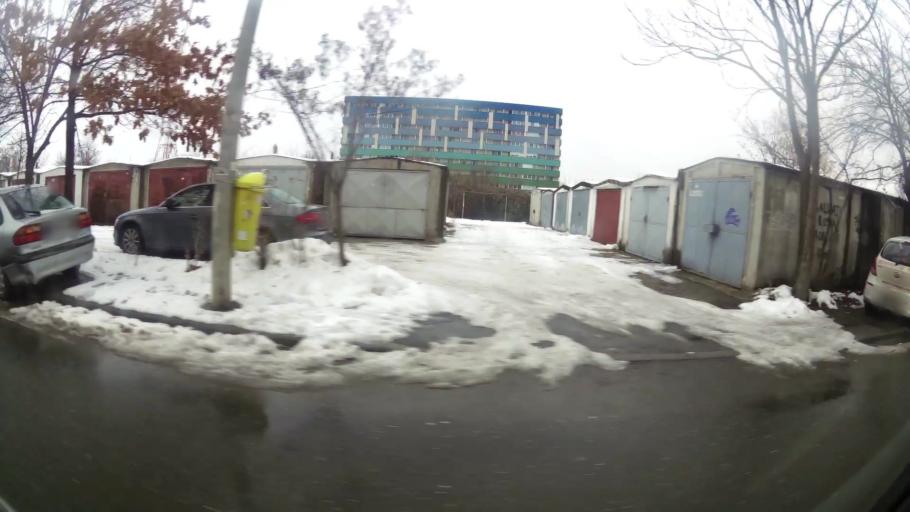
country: RO
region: Ilfov
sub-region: Comuna Chiajna
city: Rosu
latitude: 44.4387
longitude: 26.0392
